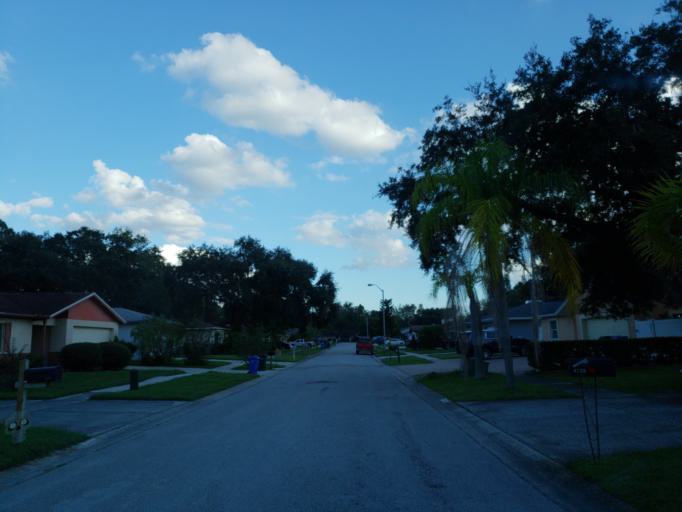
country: US
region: Florida
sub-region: Hillsborough County
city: Carrollwood Village
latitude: 28.0521
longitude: -82.5226
